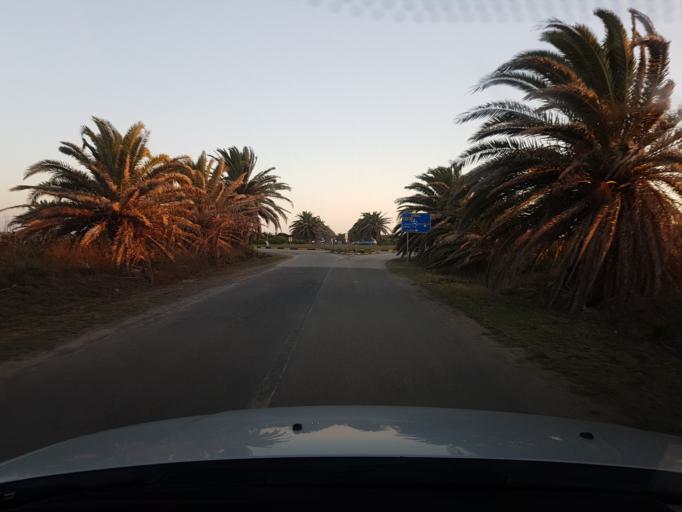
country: IT
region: Sardinia
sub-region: Provincia di Oristano
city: Riola Sardo
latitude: 40.0413
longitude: 8.4020
